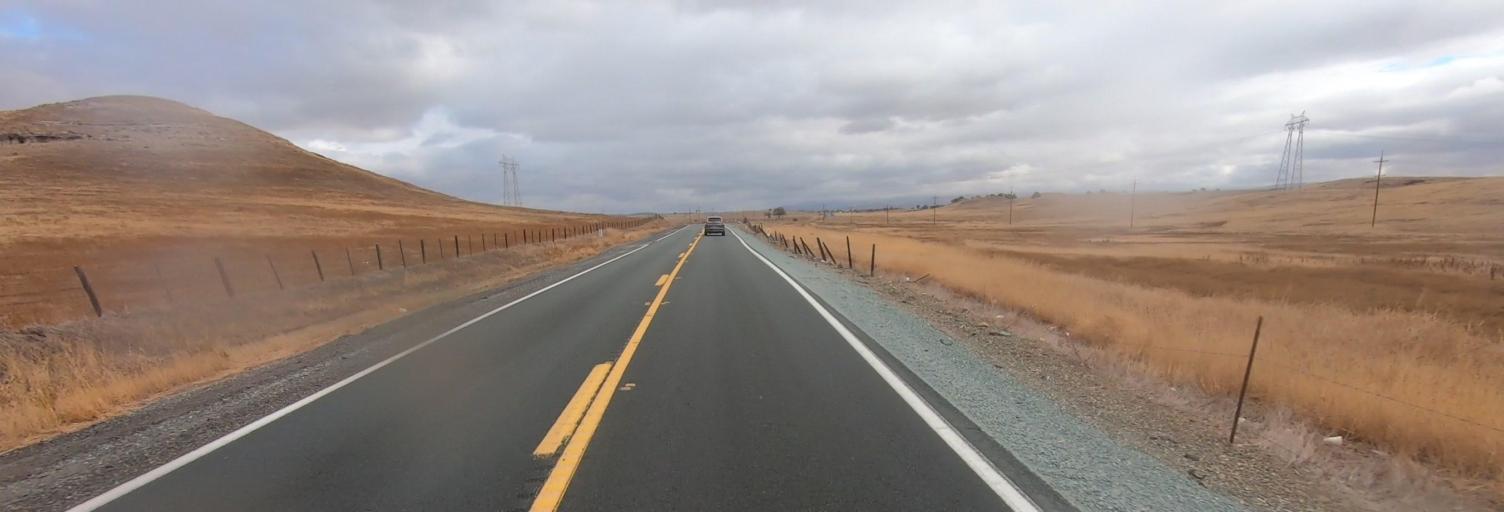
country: US
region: California
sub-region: San Joaquin County
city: Linden
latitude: 38.0789
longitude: -120.9757
